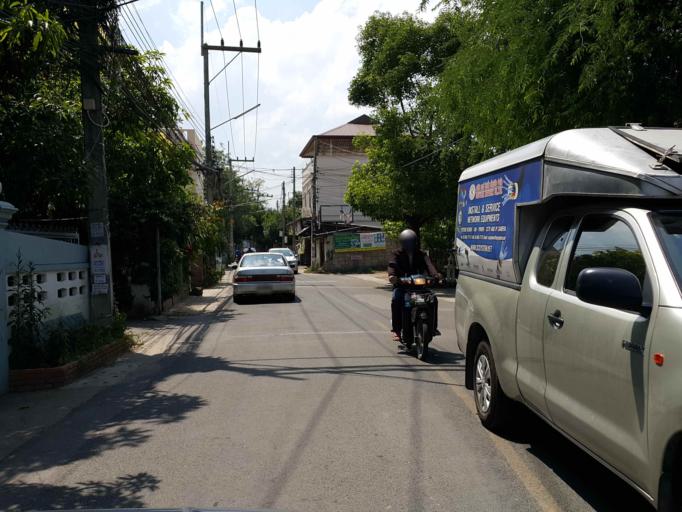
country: TH
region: Chiang Mai
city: Chiang Mai
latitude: 18.7915
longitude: 99.0254
